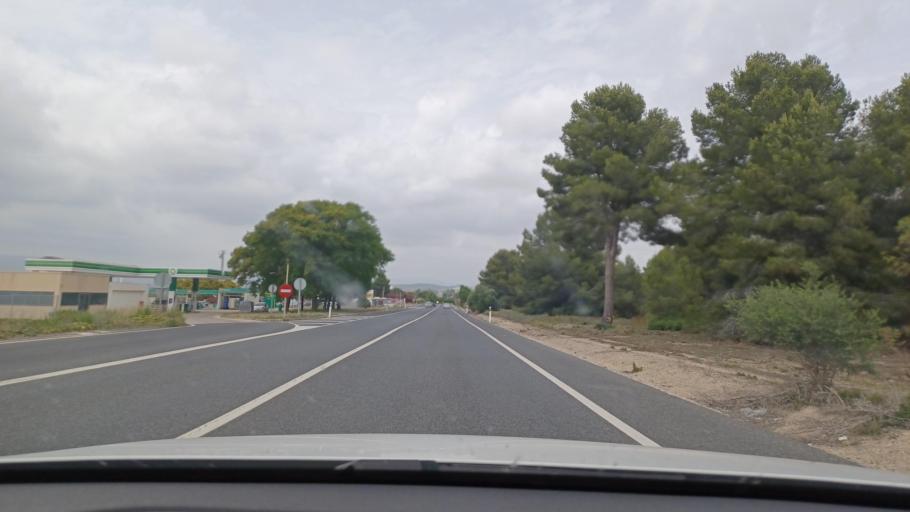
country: ES
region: Catalonia
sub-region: Provincia de Tarragona
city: la Pobla de Mafumet
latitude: 41.1727
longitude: 1.2398
